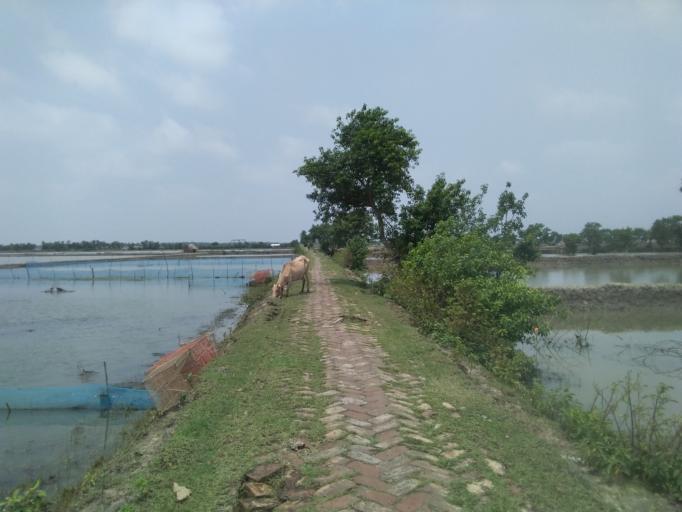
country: BD
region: Khulna
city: Phultala
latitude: 22.6421
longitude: 89.4170
